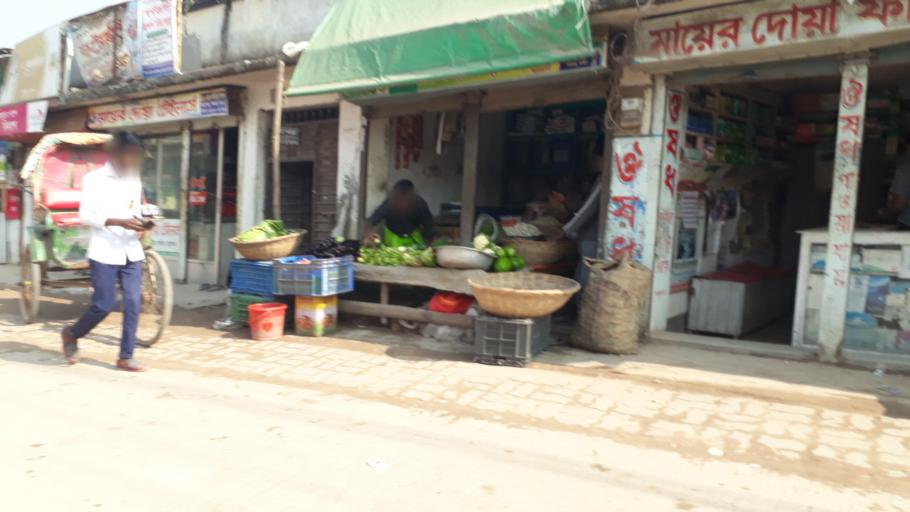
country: BD
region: Dhaka
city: Tungi
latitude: 23.8529
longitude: 90.2498
